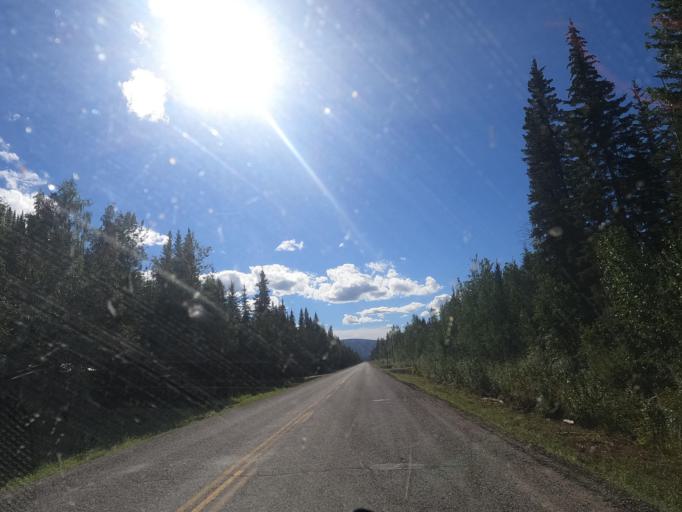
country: CA
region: Yukon
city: Dawson City
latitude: 64.0594
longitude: -139.0833
